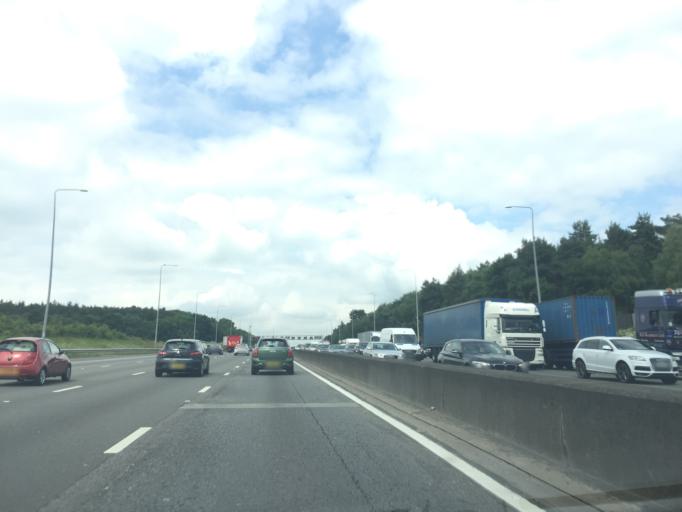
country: GB
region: England
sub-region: Buckinghamshire
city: Gerrards Cross
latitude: 51.5905
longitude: -0.5333
